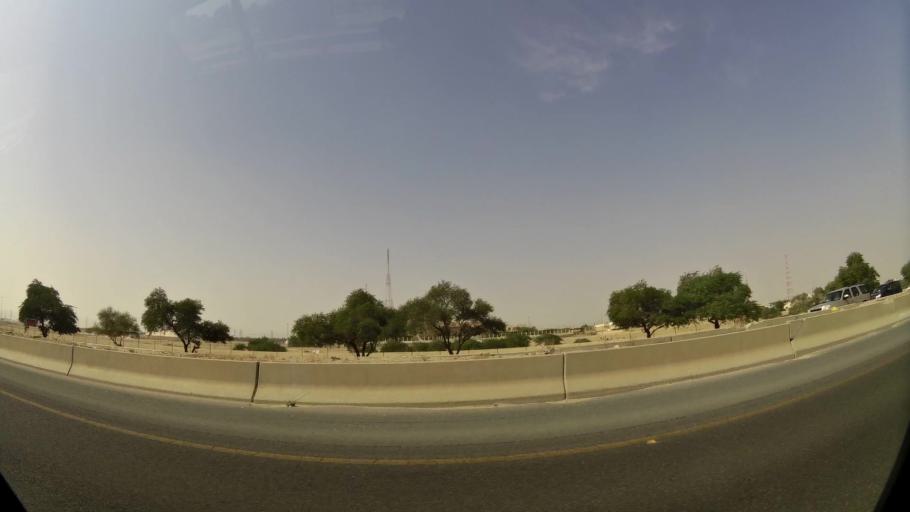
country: KW
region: Al Ahmadi
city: Al Fahahil
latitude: 29.0798
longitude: 48.1135
